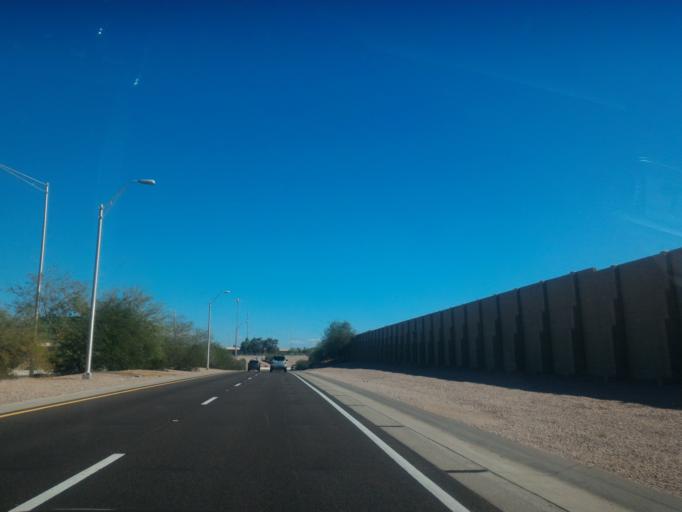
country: US
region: Arizona
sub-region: Maricopa County
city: Tempe
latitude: 33.3854
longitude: -111.8964
